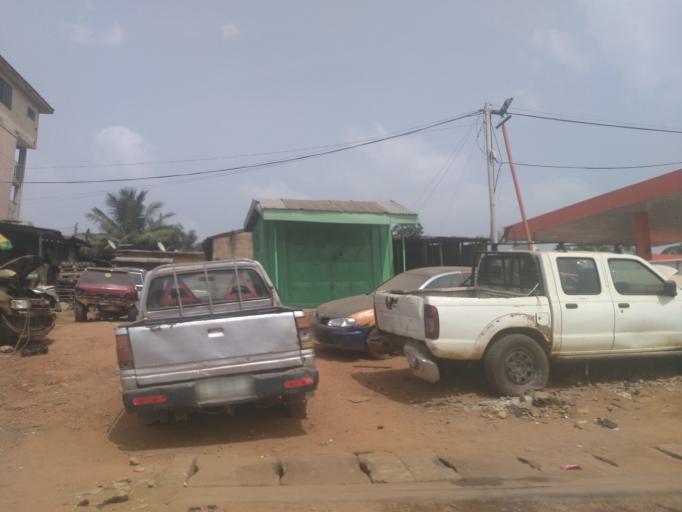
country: GH
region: Greater Accra
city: Dome
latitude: 5.6089
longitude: -0.2410
